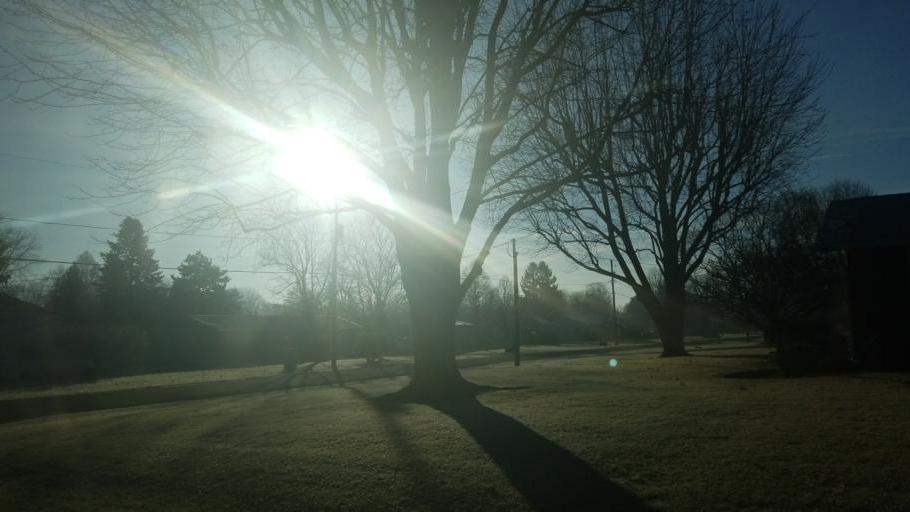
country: US
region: Ohio
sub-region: Marion County
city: Marion
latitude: 40.5782
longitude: -83.1041
